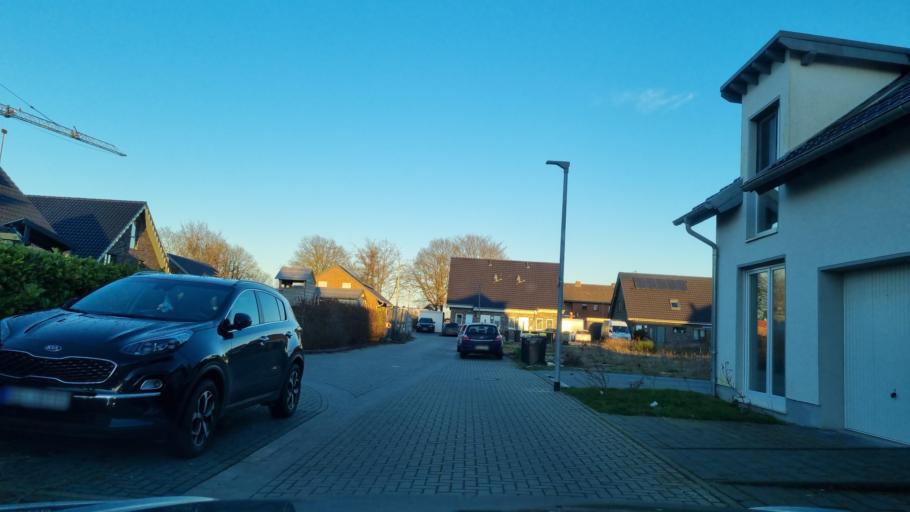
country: DE
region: North Rhine-Westphalia
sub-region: Regierungsbezirk Dusseldorf
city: Kranenburg
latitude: 51.7860
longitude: 6.0640
